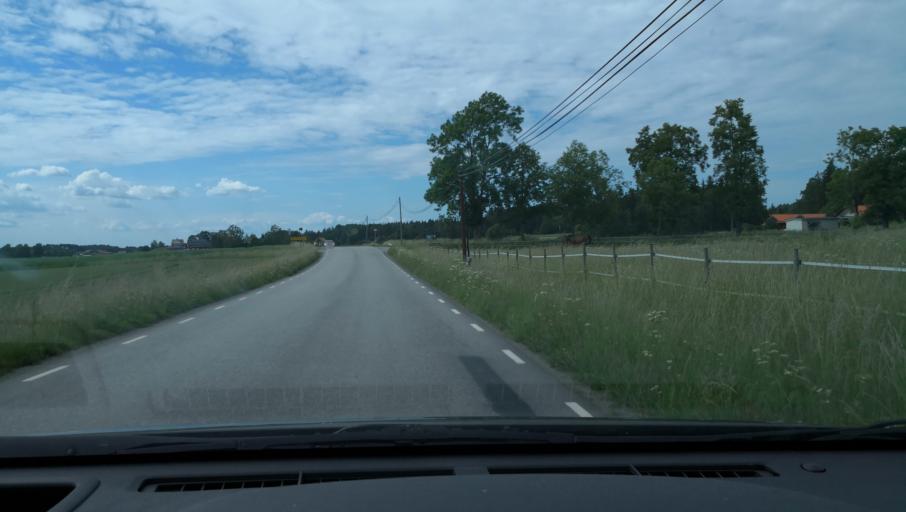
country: SE
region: Uppsala
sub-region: Uppsala Kommun
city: Uppsala
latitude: 59.8056
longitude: 17.5314
